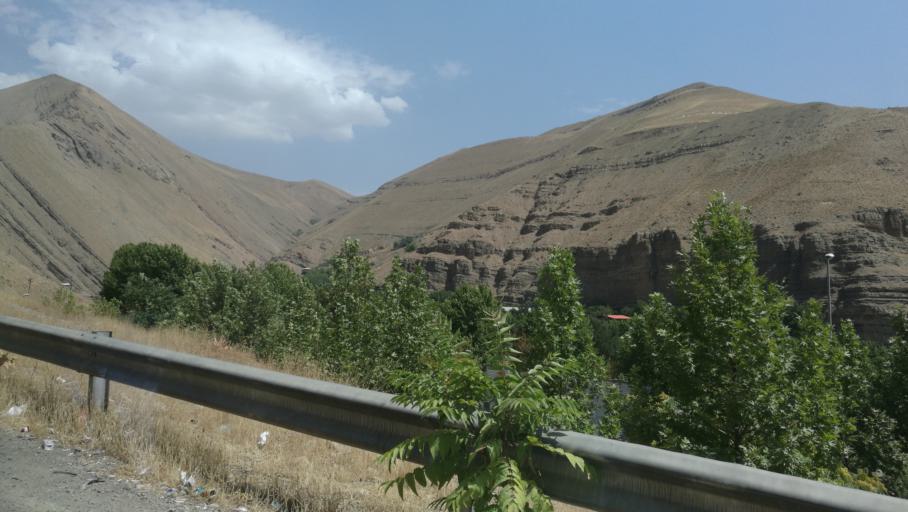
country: IR
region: Alborz
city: Karaj
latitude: 35.9451
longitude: 51.0766
